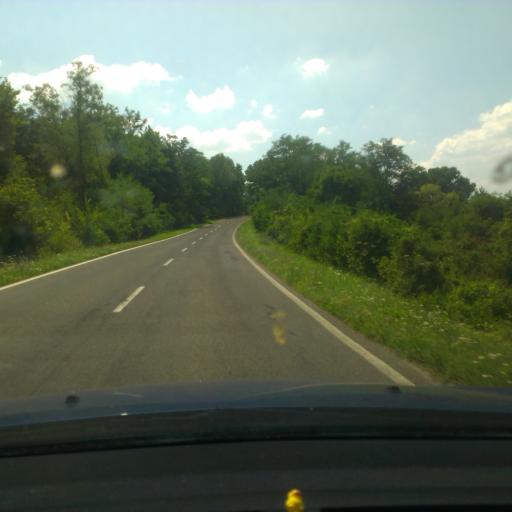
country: SK
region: Trnavsky
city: Hlohovec
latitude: 48.4907
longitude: 17.8132
